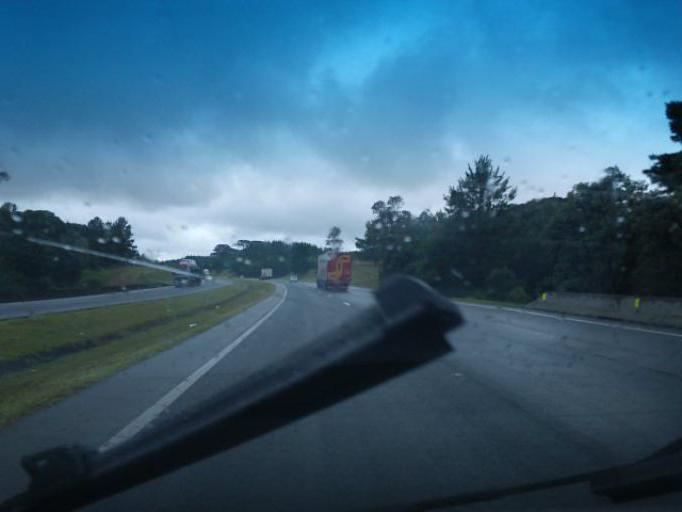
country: BR
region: Parana
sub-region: Piraquara
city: Piraquara
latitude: -25.4758
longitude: -49.0959
